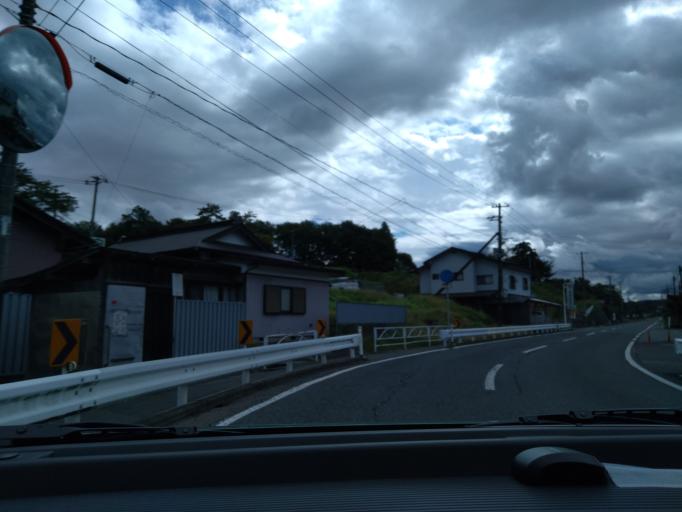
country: JP
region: Iwate
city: Ichinoseki
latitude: 38.8998
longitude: 141.1307
